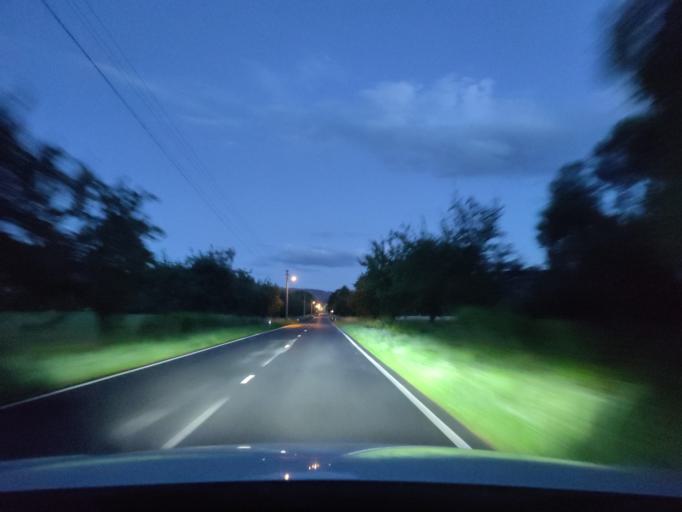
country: CZ
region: Olomoucky
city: Zlate Hory
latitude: 50.2730
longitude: 17.3928
